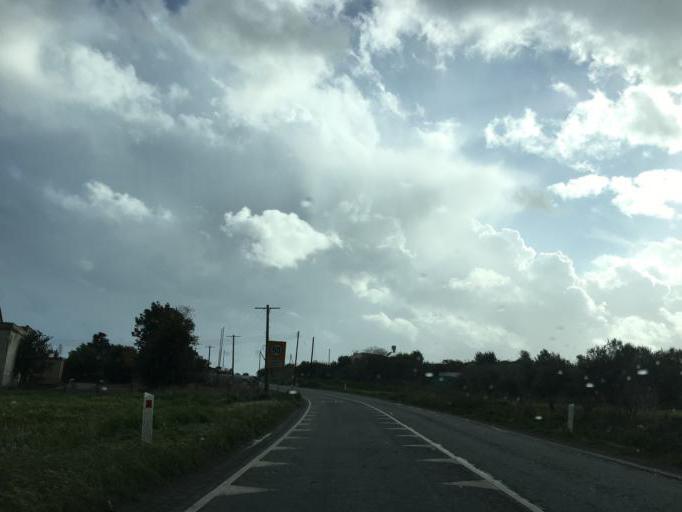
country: CY
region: Limassol
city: Erimi
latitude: 34.6728
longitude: 32.9129
